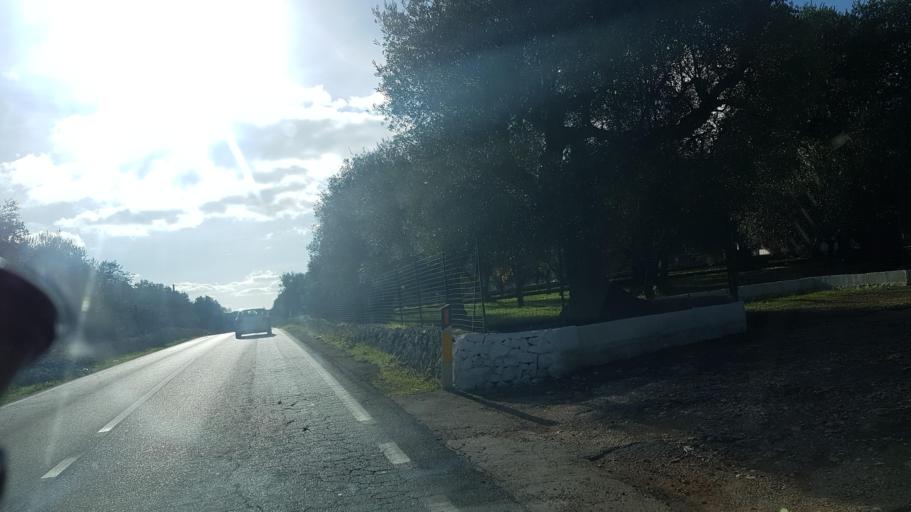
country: IT
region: Apulia
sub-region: Provincia di Brindisi
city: Ostuni
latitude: 40.6874
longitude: 17.5512
